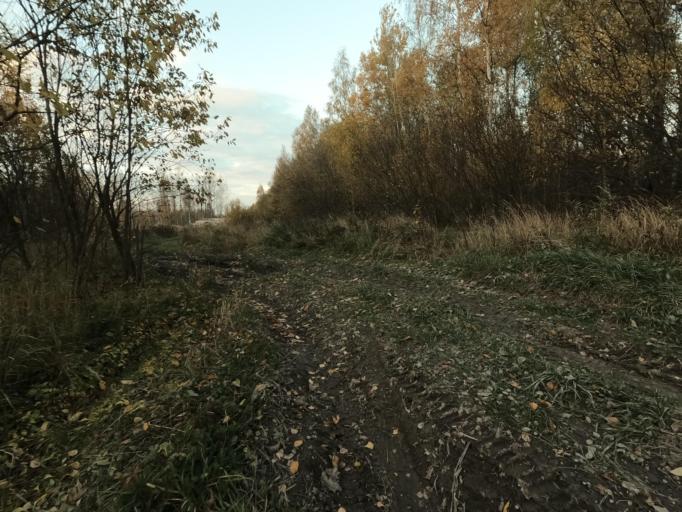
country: RU
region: Leningrad
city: Mga
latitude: 59.8159
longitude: 31.1778
